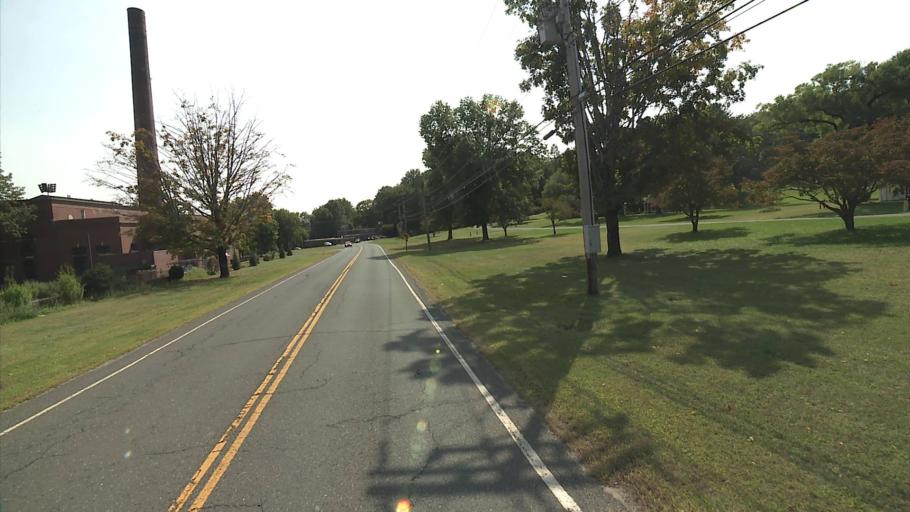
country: US
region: Connecticut
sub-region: New Haven County
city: Heritage Village
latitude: 41.4911
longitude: -73.2610
